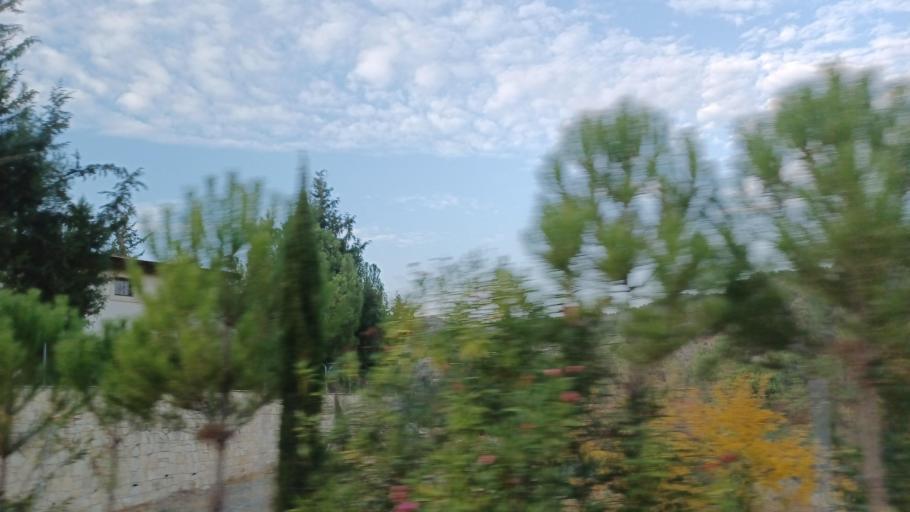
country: CY
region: Limassol
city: Pelendri
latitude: 34.8534
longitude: 32.9476
